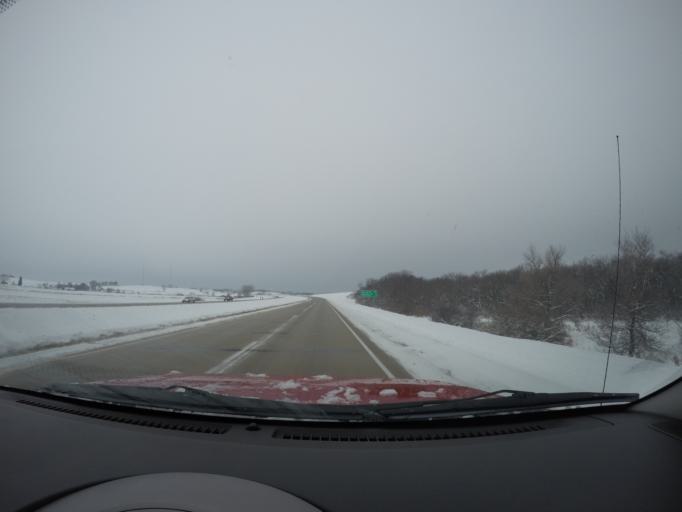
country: US
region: Minnesota
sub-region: Olmsted County
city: Rochester
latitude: 43.9690
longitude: -92.3988
